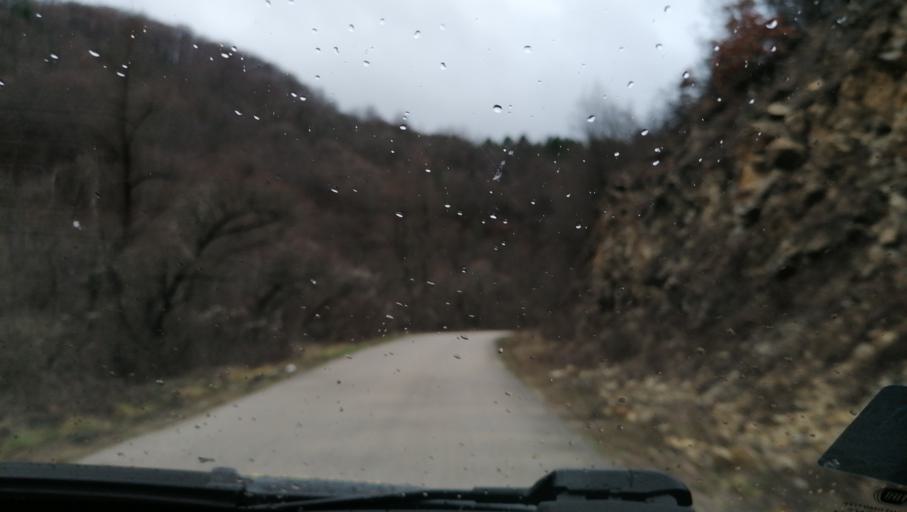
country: RS
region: Central Serbia
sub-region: Pirotski Okrug
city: Dimitrovgrad
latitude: 42.9782
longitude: 22.6514
